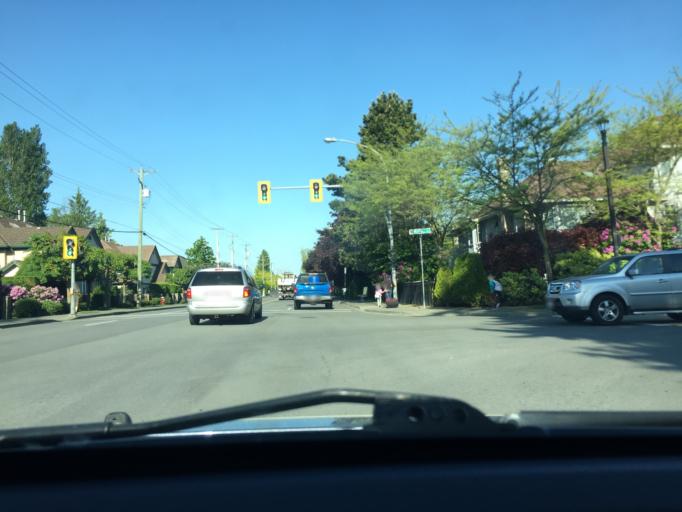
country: CA
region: British Columbia
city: Richmond
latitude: 49.1556
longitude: -123.1433
